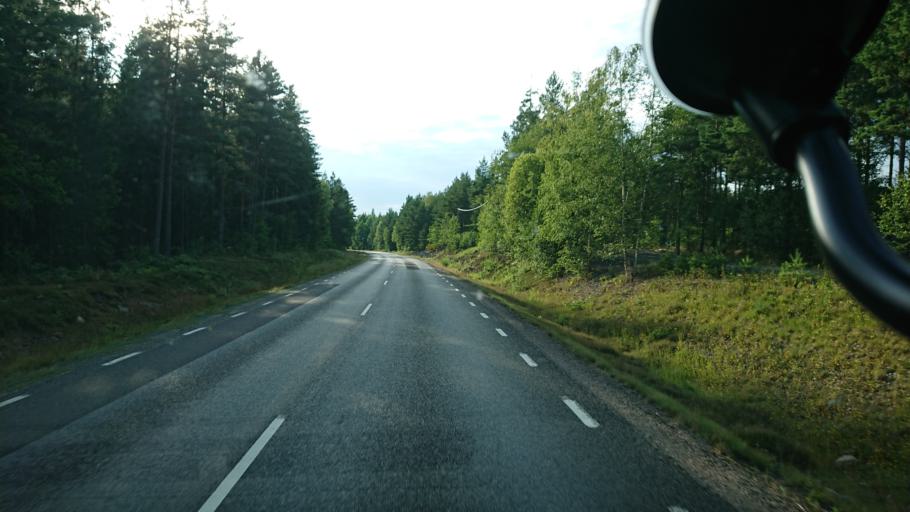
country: SE
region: Kronoberg
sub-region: Vaxjo Kommun
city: Rottne
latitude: 57.0309
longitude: 14.9710
